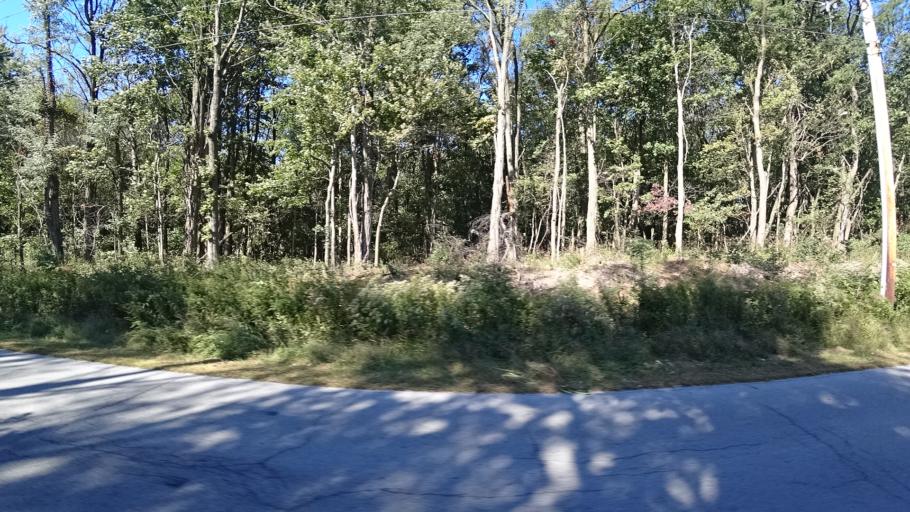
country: US
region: Indiana
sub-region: LaPorte County
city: Michigan City
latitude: 41.6837
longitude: -86.9014
